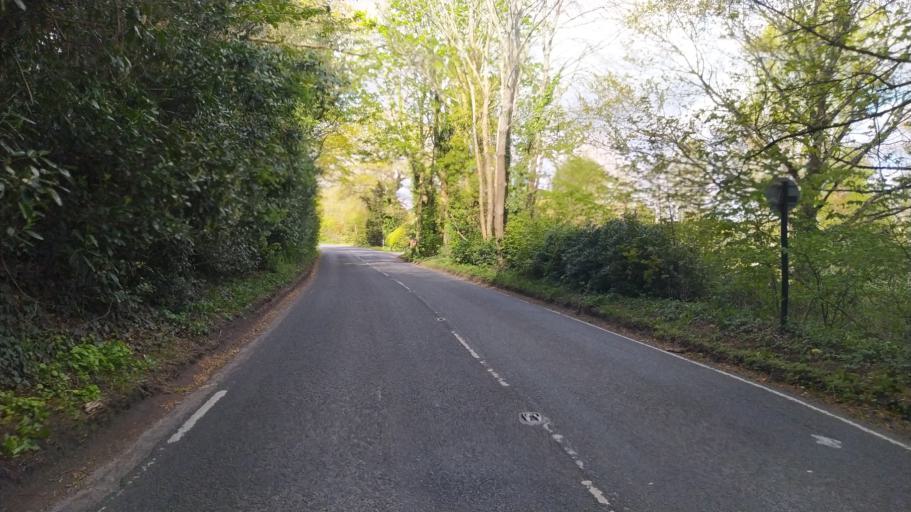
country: GB
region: England
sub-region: Hampshire
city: Marchwood
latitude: 50.8742
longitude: -1.4362
